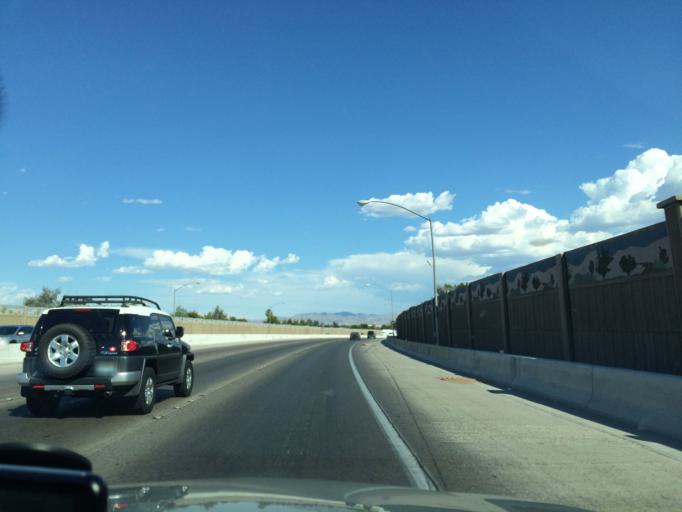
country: US
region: Nevada
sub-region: Clark County
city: North Las Vegas
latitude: 36.1659
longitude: -115.0963
